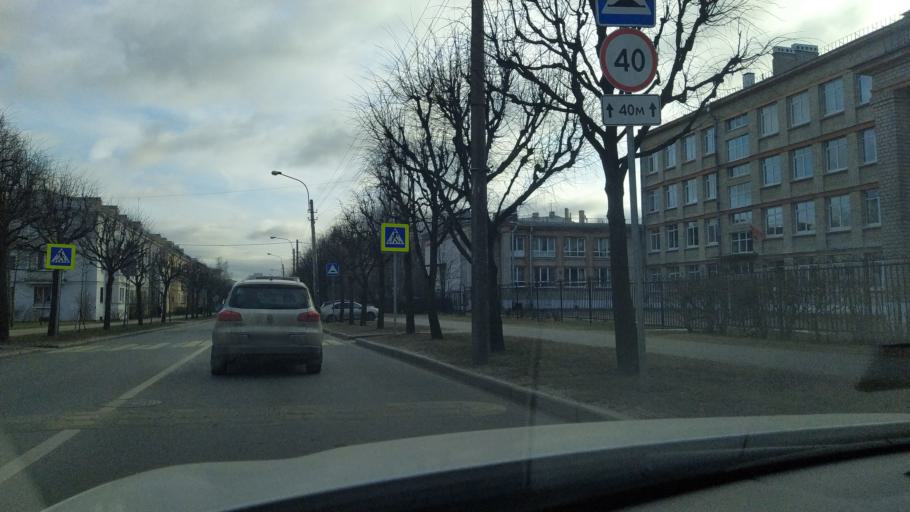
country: RU
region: St.-Petersburg
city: Pushkin
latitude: 59.7246
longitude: 30.4235
